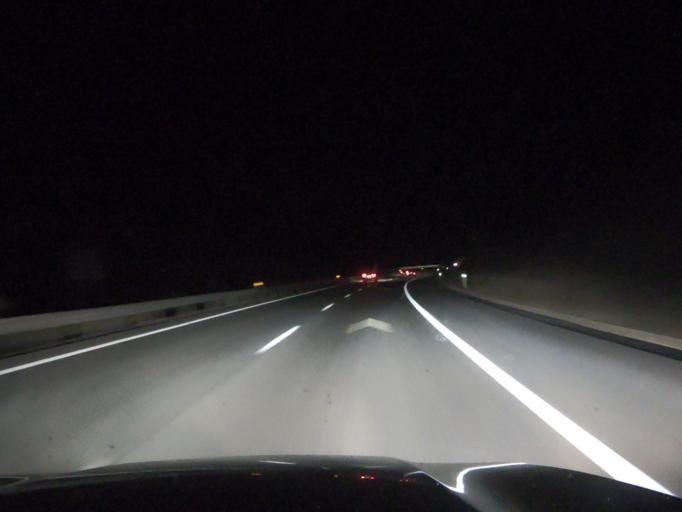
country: PT
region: Faro
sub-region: Silves
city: Sao Bartolomeu de Messines
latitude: 37.2844
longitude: -8.2663
